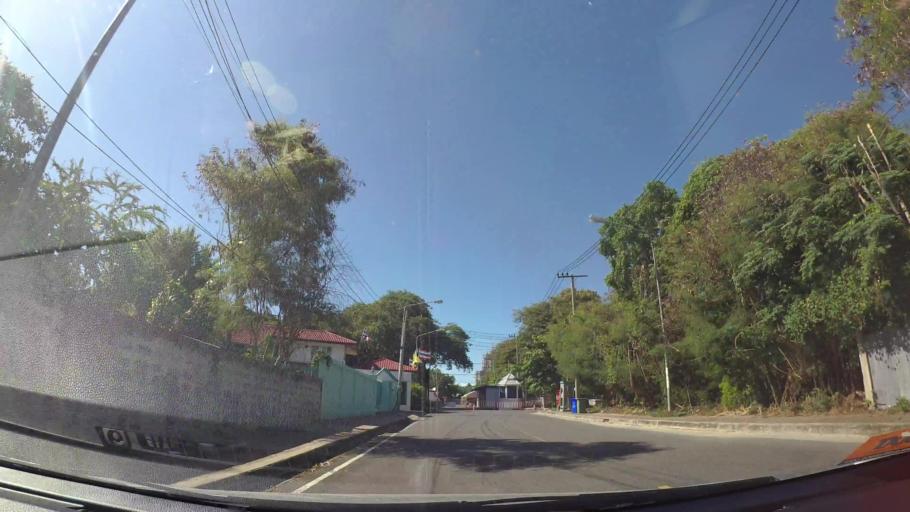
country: TH
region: Chon Buri
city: Phatthaya
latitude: 12.9117
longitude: 100.8569
